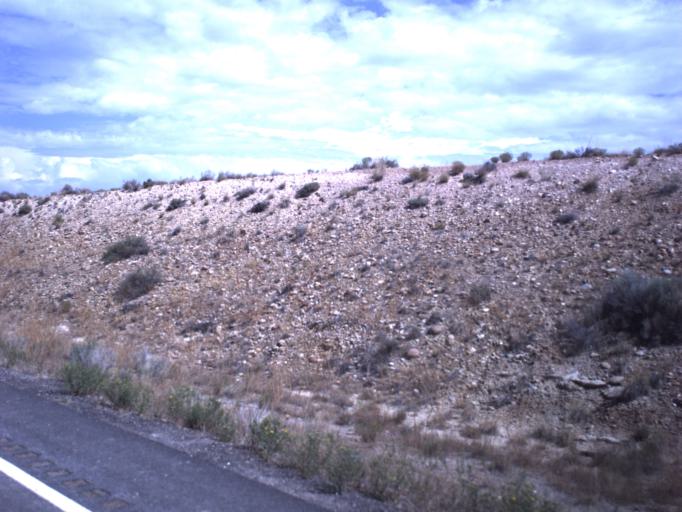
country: US
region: Utah
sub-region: Uintah County
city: Naples
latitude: 40.2725
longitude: -109.4605
